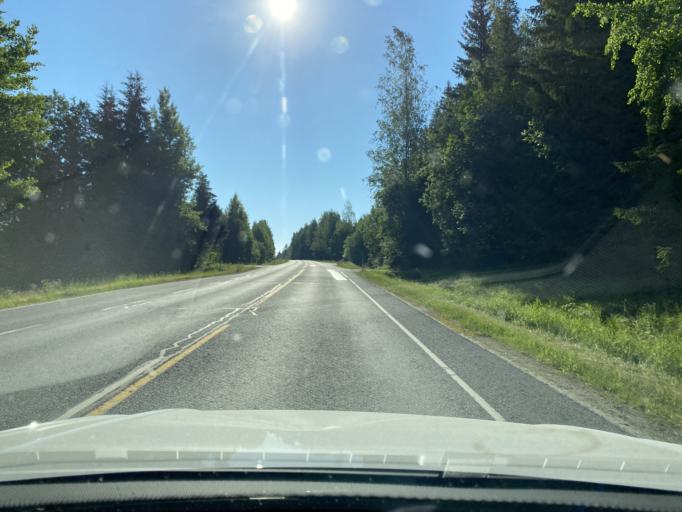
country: FI
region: Haeme
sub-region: Forssa
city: Tammela
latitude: 60.8267
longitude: 23.9057
